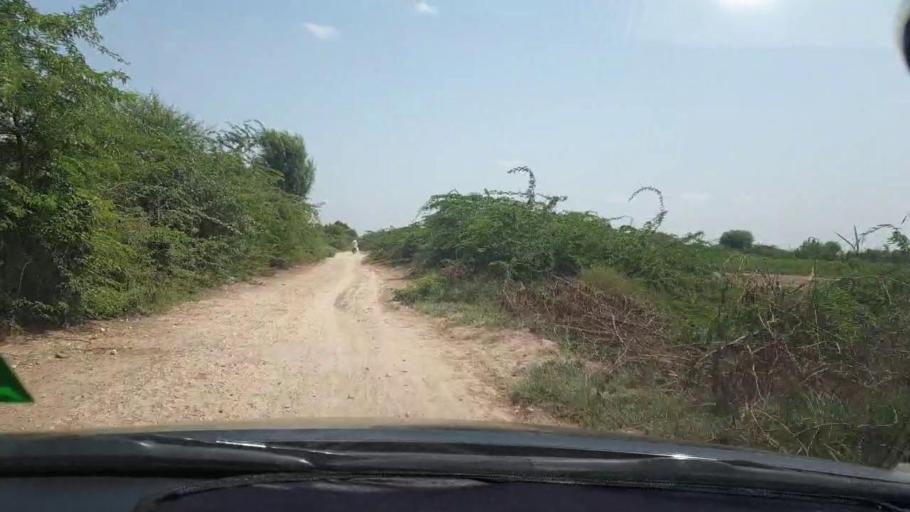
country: PK
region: Sindh
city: Tando Bago
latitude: 24.8963
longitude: 69.0837
